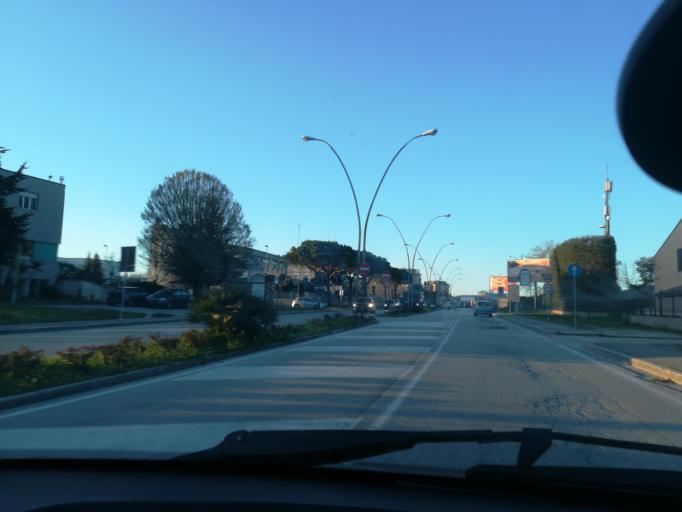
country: IT
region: The Marches
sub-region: Provincia di Macerata
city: Portocivitanova
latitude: 43.2952
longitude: 13.7364
